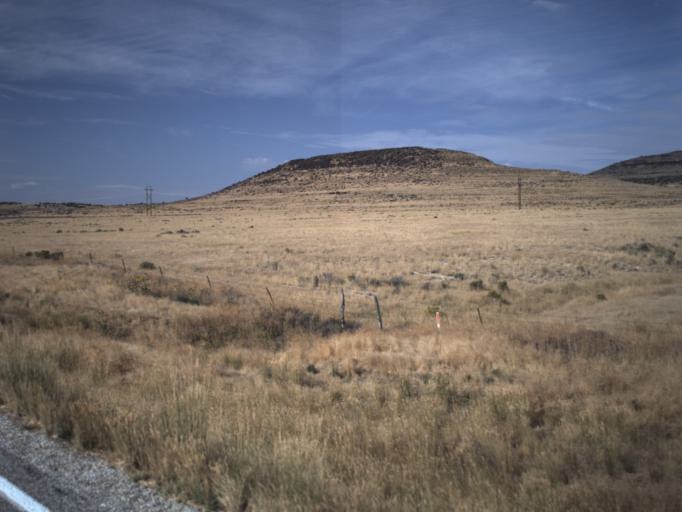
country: US
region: Idaho
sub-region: Minidoka County
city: Rupert
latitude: 41.8448
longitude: -113.1384
